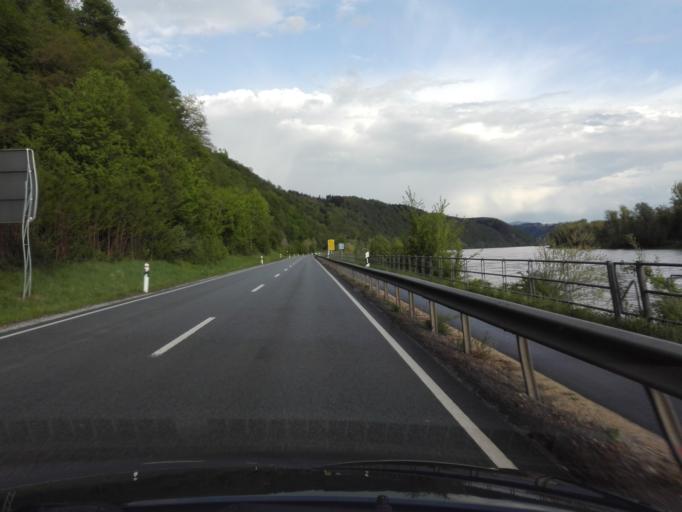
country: DE
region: Bavaria
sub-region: Lower Bavaria
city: Thyrnau
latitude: 48.5911
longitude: 13.5173
